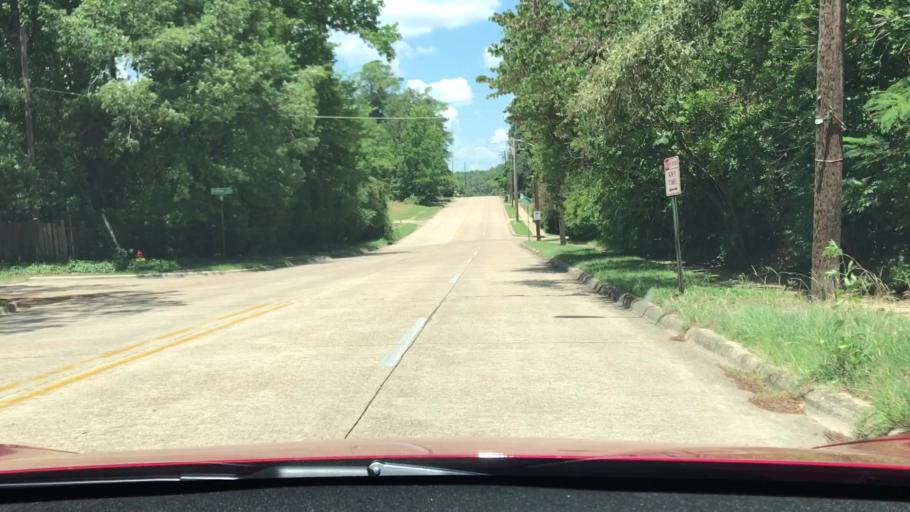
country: US
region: Louisiana
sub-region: Bossier Parish
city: Bossier City
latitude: 32.4386
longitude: -93.7348
